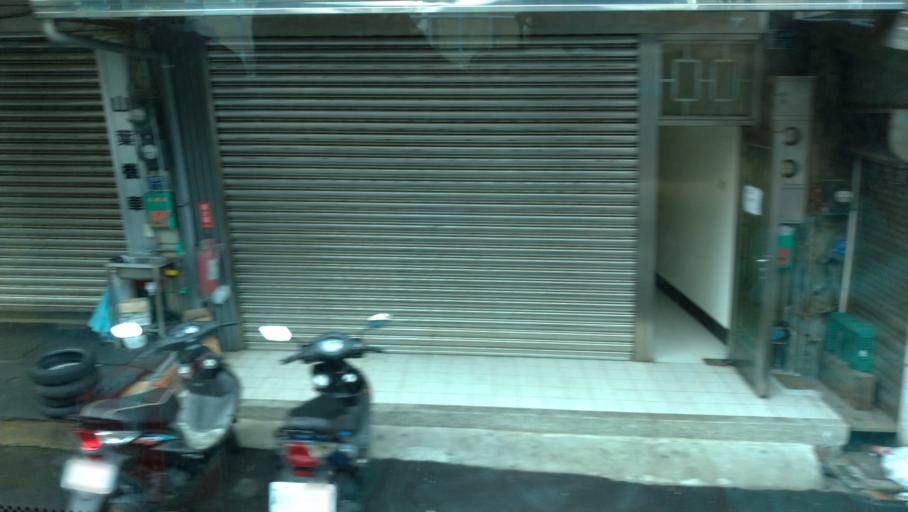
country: TW
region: Taiwan
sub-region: Keelung
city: Keelung
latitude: 25.1511
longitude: 121.7729
